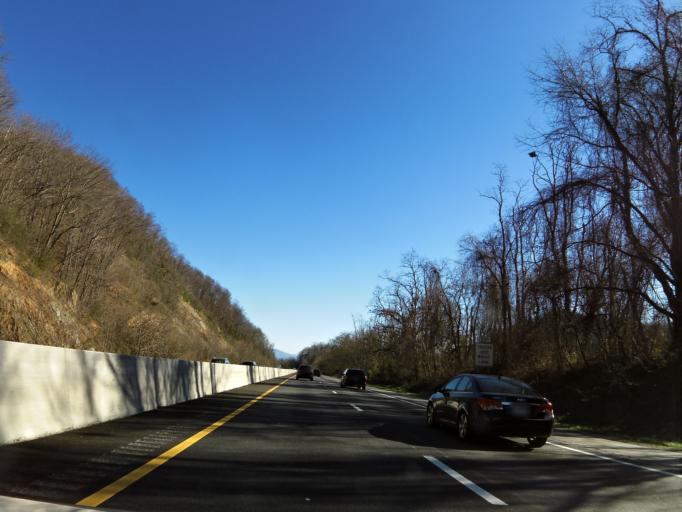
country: US
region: North Carolina
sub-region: Haywood County
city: Canton
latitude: 35.5399
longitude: -82.7887
